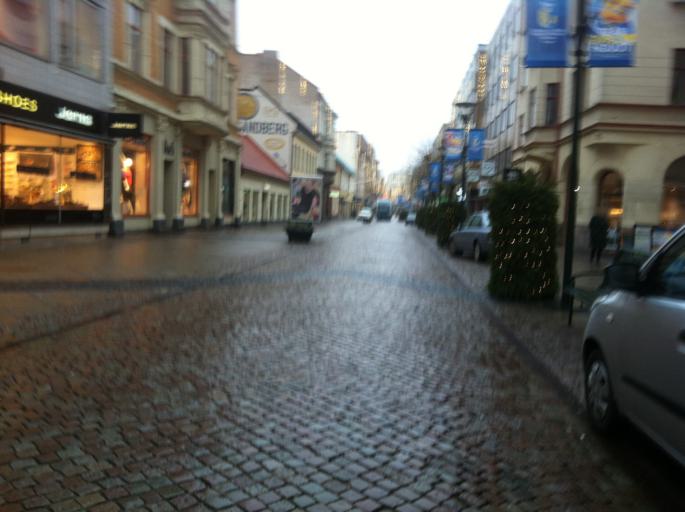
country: SE
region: Skane
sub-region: Malmo
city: Malmoe
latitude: 55.5972
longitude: 13.0008
